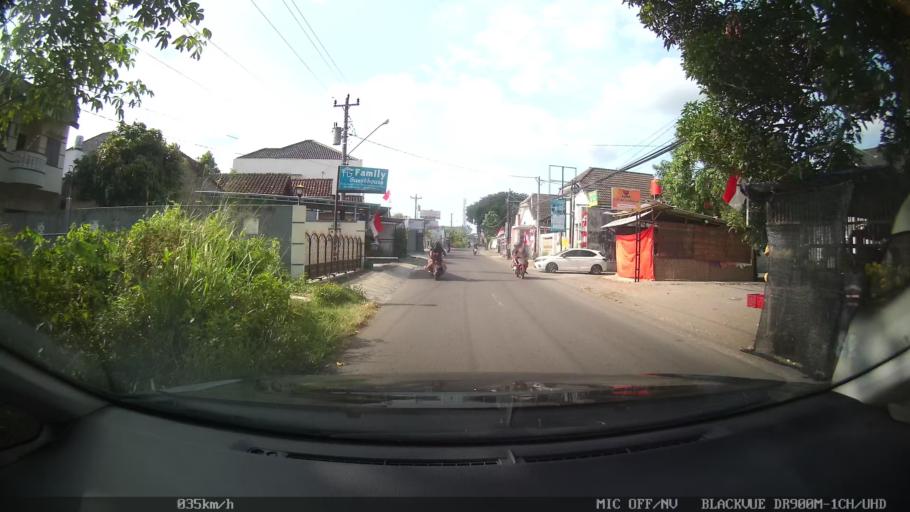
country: ID
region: Daerah Istimewa Yogyakarta
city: Depok
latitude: -7.7415
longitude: 110.4512
